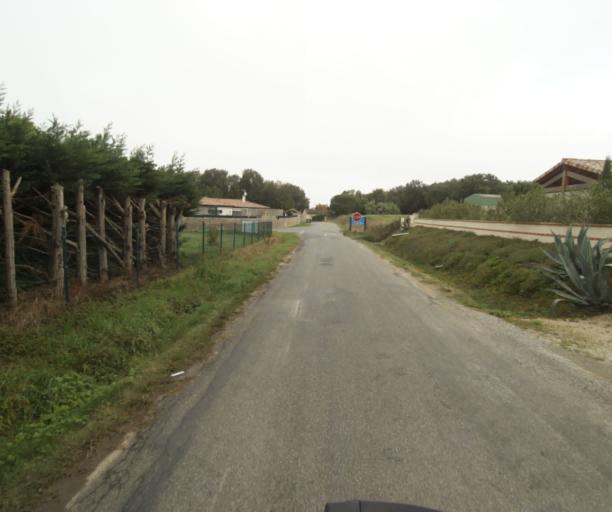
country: FR
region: Midi-Pyrenees
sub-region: Departement du Tarn-et-Garonne
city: Labastide-Saint-Pierre
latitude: 43.8851
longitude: 1.3806
